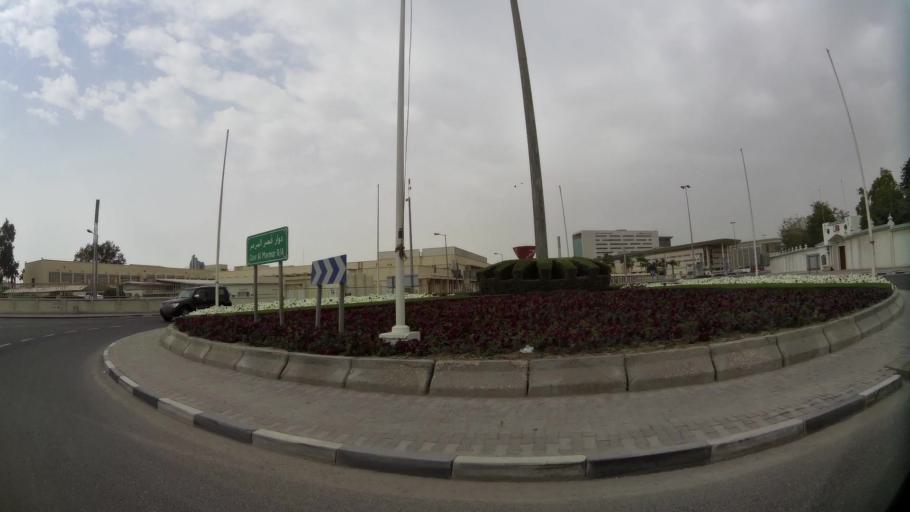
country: QA
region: Baladiyat ad Dawhah
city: Doha
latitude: 25.2937
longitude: 51.5140
